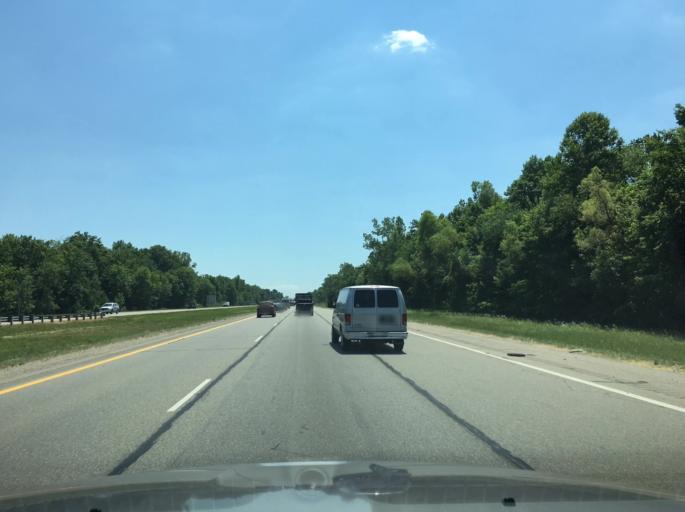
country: US
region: Michigan
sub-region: Macomb County
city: Shelby
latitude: 42.6651
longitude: -83.0147
